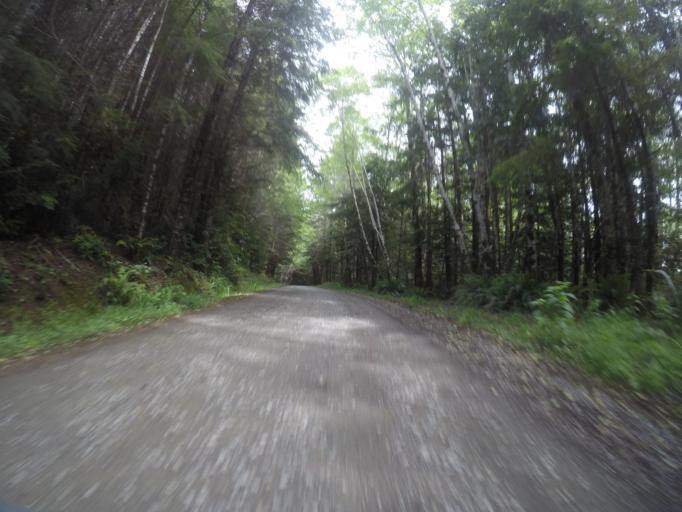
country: US
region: California
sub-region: Humboldt County
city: Westhaven-Moonstone
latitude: 41.2225
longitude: -124.0025
